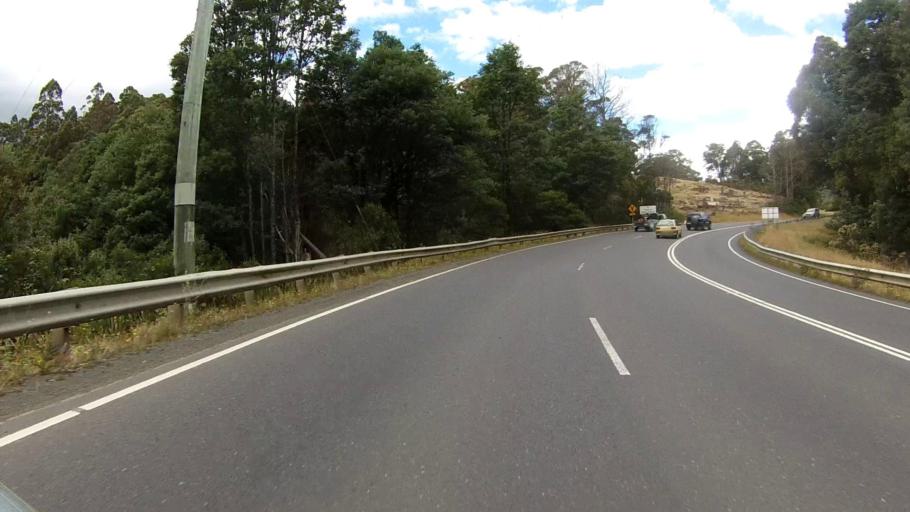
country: AU
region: Tasmania
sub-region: Huon Valley
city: Huonville
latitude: -42.9747
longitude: 147.1469
